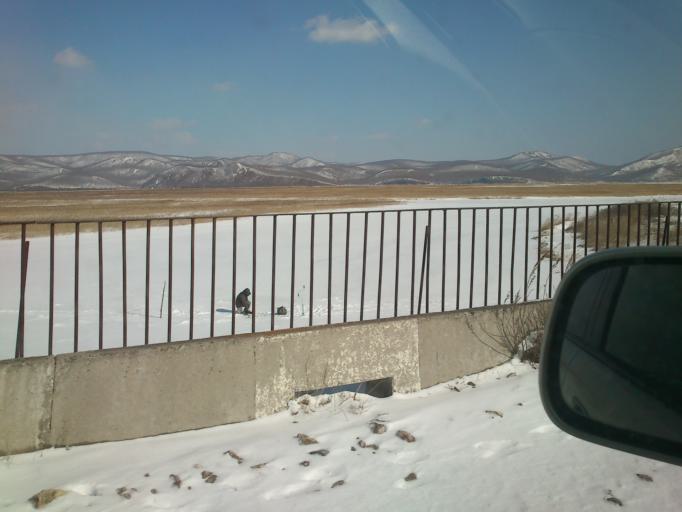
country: RU
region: Primorskiy
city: Rudnaya Pristan'
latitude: 44.1664
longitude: 135.6272
